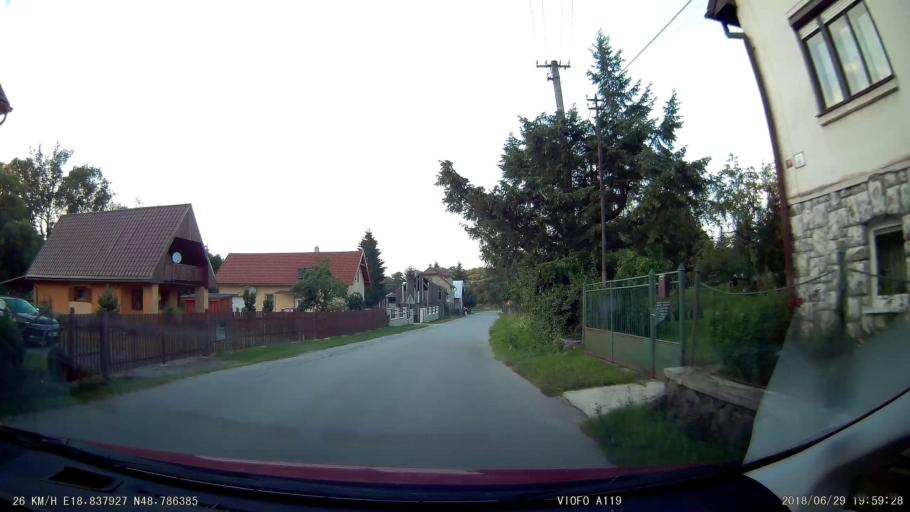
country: SK
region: Nitriansky
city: Handlova
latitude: 48.7864
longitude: 18.8380
